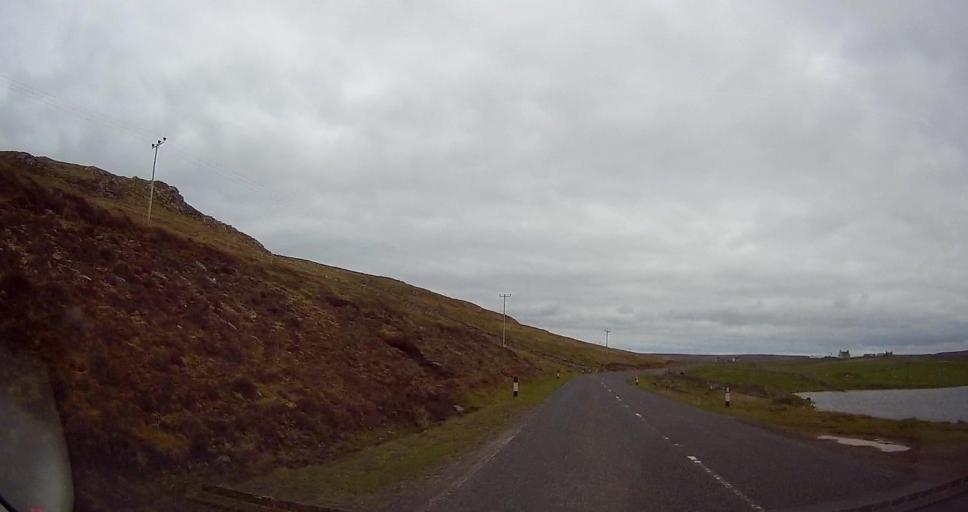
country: GB
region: Scotland
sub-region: Shetland Islands
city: Shetland
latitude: 60.6922
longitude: -0.9567
